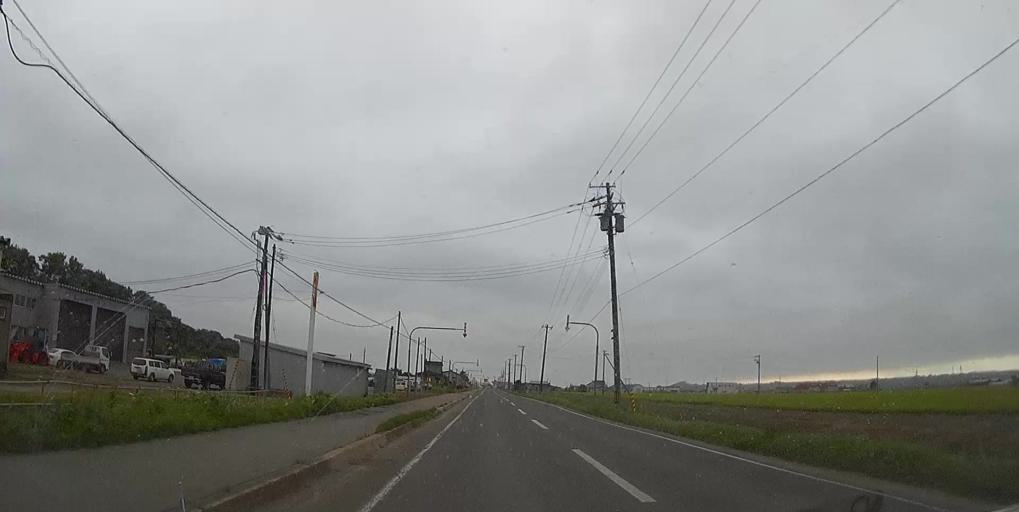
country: JP
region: Hokkaido
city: Iwanai
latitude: 42.4158
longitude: 140.0163
